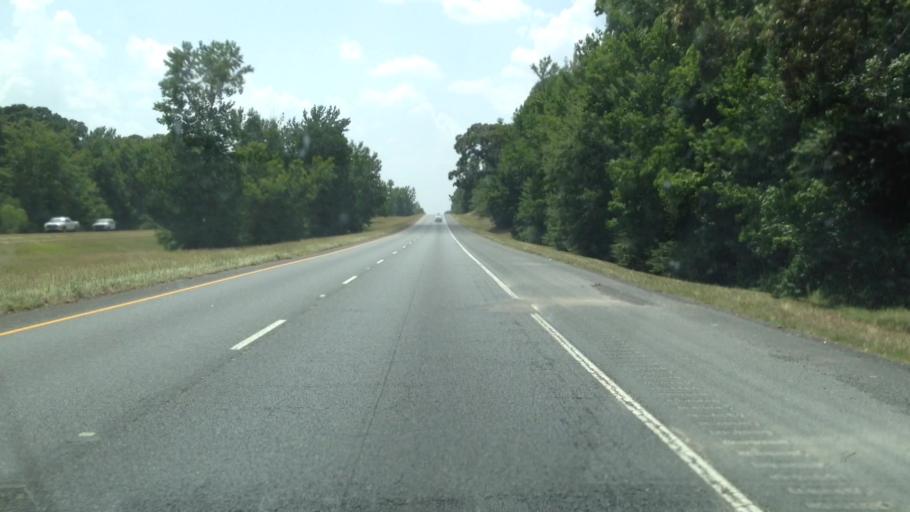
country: US
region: Louisiana
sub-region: Lincoln Parish
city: Grambling
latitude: 32.5452
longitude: -92.7475
